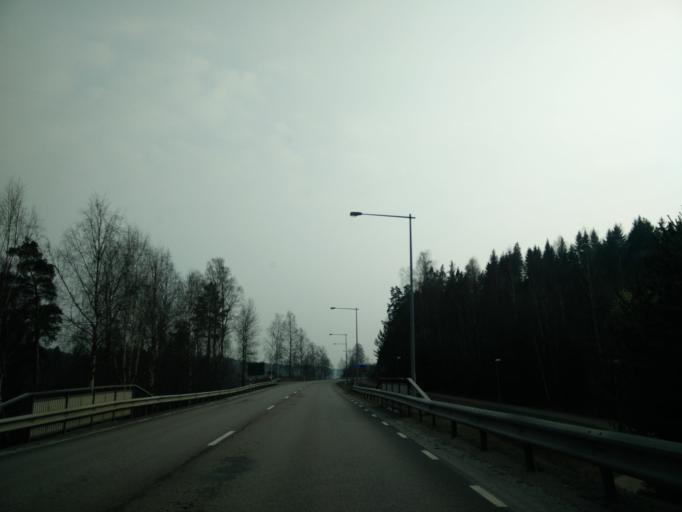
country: SE
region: Vaermland
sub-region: Forshaga Kommun
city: Forshaga
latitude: 59.5214
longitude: 13.4478
